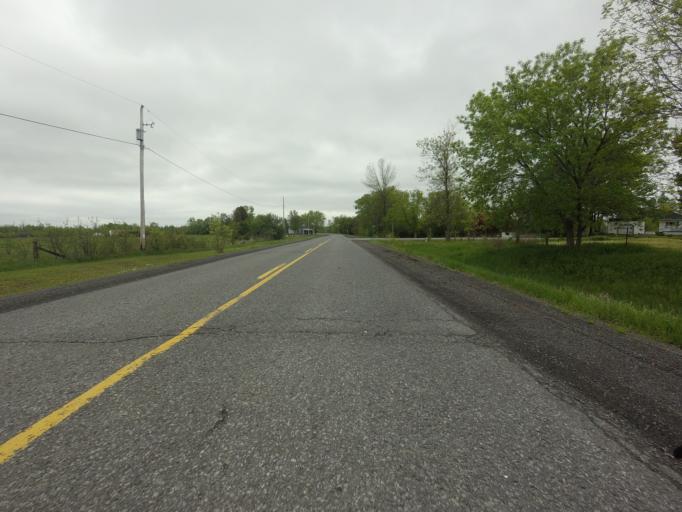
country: US
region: New York
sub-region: St. Lawrence County
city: Norfolk
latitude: 44.9619
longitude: -75.1514
